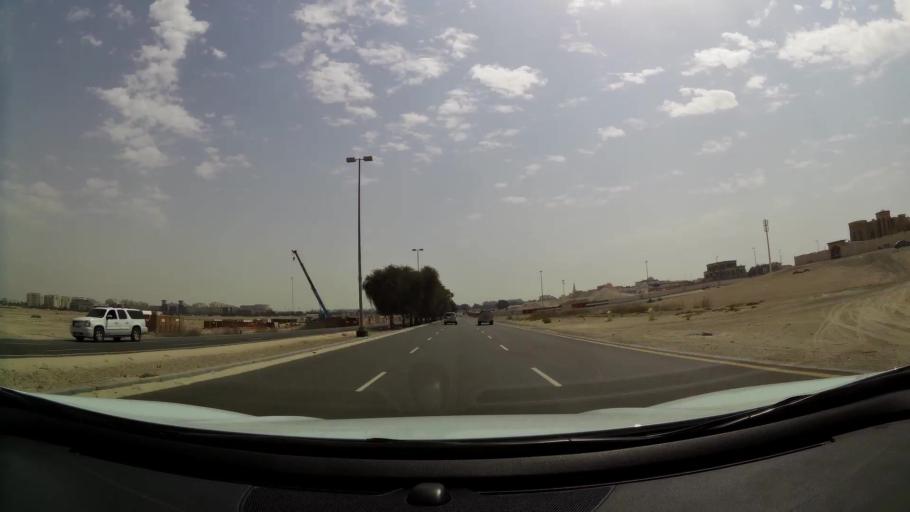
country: AE
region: Abu Dhabi
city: Abu Dhabi
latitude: 24.3123
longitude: 54.6115
